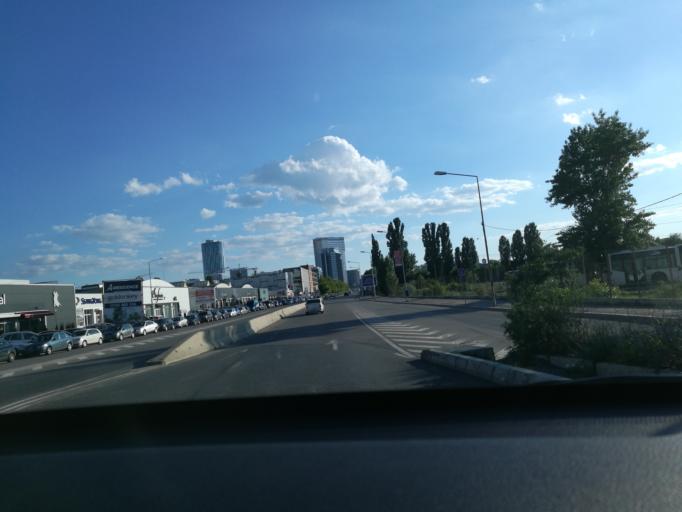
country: RO
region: Bucuresti
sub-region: Municipiul Bucuresti
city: Bucharest
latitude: 44.4859
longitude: 26.1127
